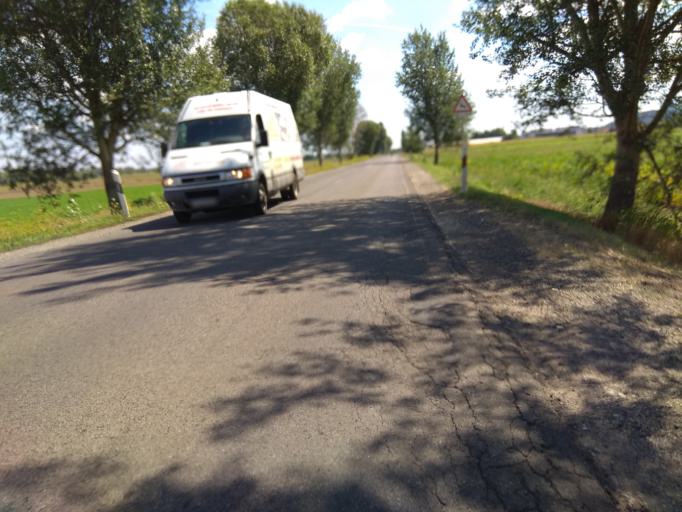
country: HU
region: Borsod-Abauj-Zemplen
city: Sajokaza
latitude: 48.2660
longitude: 20.6024
